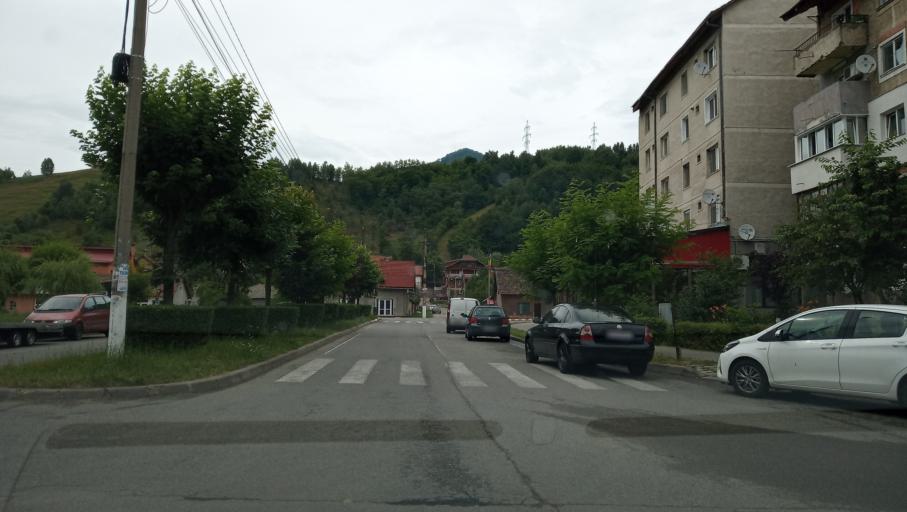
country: RO
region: Hunedoara
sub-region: Municipiul Petrosani
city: Petrosani
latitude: 45.4414
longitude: 23.3735
